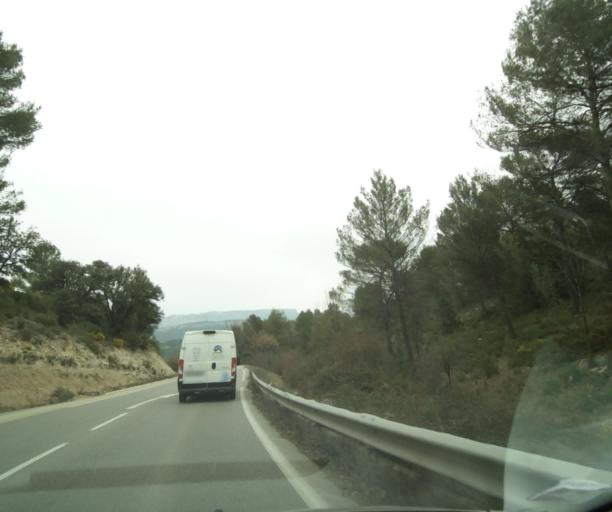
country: FR
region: Provence-Alpes-Cote d'Azur
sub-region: Departement des Bouches-du-Rhone
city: Fuveau
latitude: 43.4683
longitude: 5.5455
